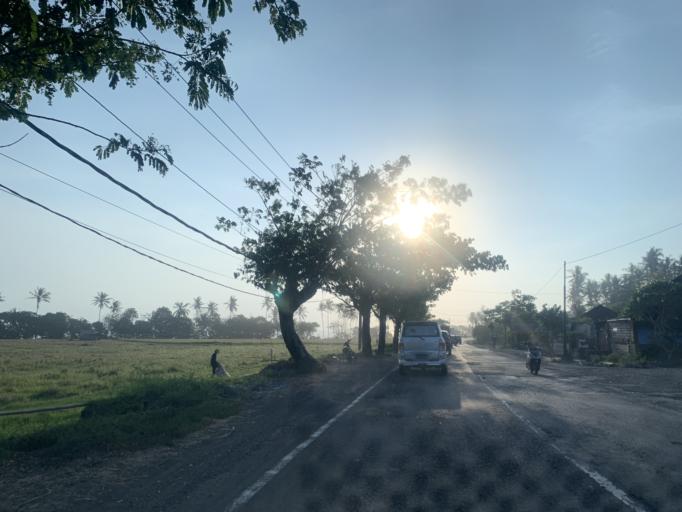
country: ID
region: Bali
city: Angkahgede
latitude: -8.4779
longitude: 114.9389
